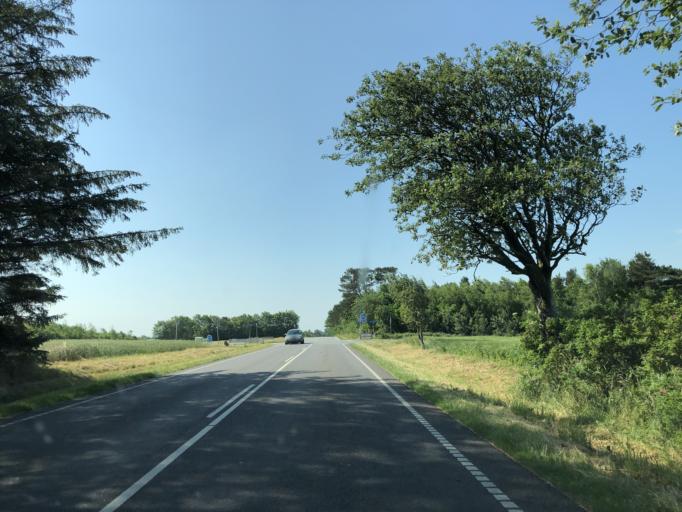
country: DK
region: South Denmark
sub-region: Varde Kommune
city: Varde
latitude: 55.6622
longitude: 8.4900
